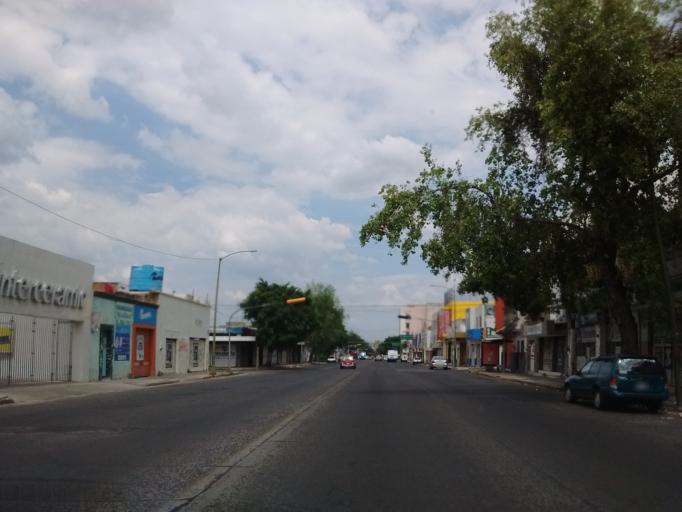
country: MX
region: Jalisco
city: Guadalajara
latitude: 20.6663
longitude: -103.3580
